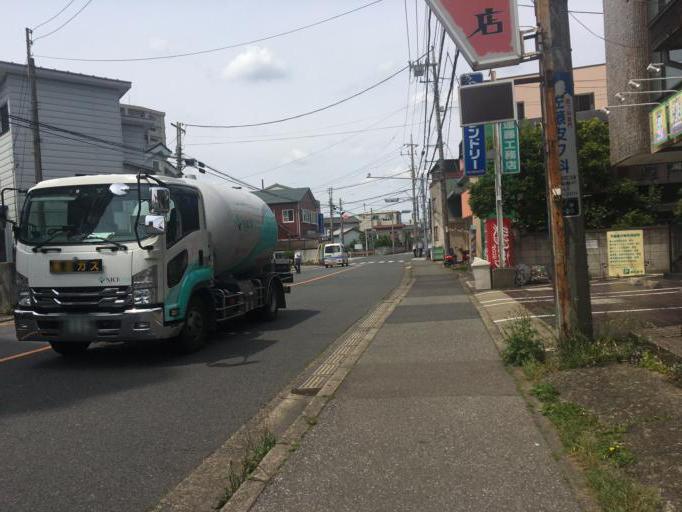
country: JP
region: Saitama
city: Shimotoda
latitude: 35.8405
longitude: 139.6603
